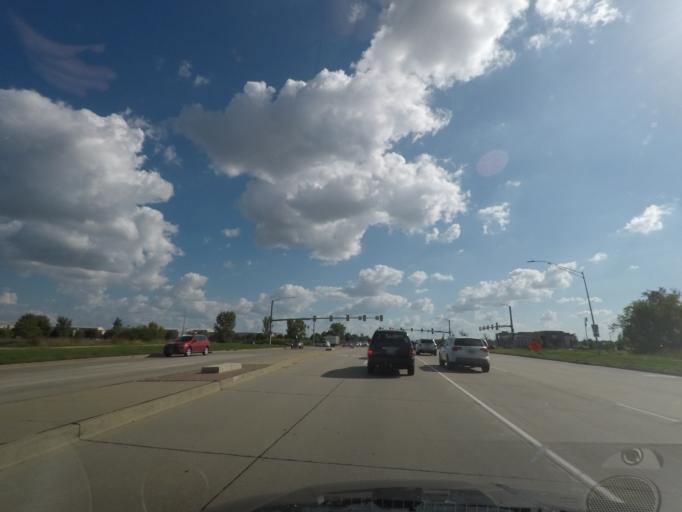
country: US
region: Iowa
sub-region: Dallas County
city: Waukee
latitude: 41.5743
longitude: -93.8093
